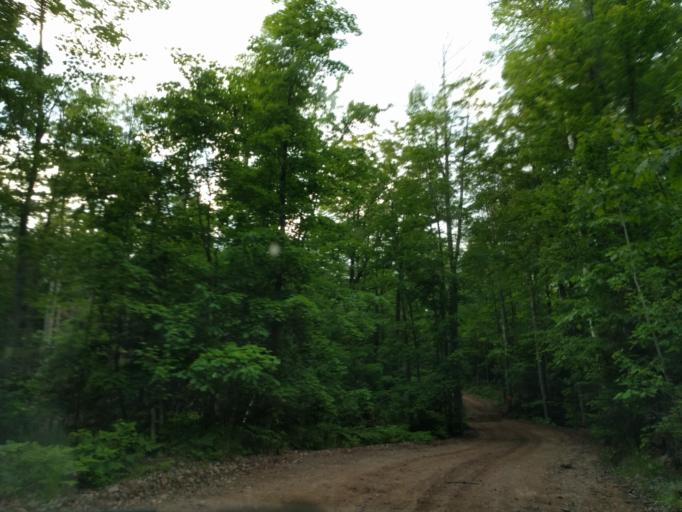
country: US
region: Michigan
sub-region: Marquette County
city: Trowbridge Park
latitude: 46.6123
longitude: -87.5110
